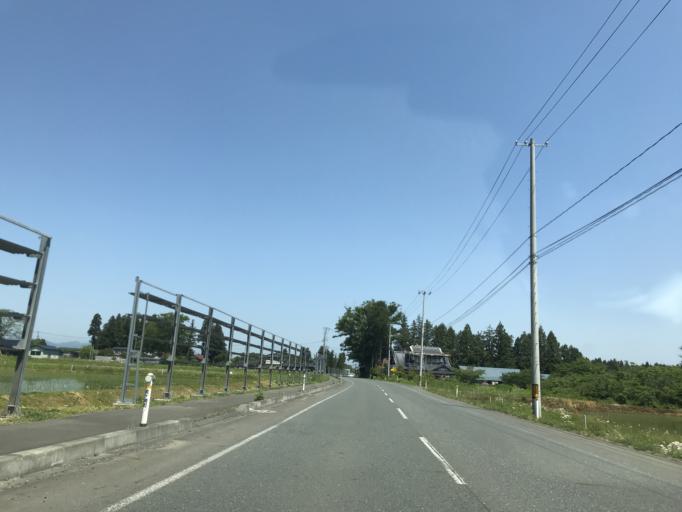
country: JP
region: Iwate
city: Kitakami
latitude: 39.2432
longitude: 141.0666
